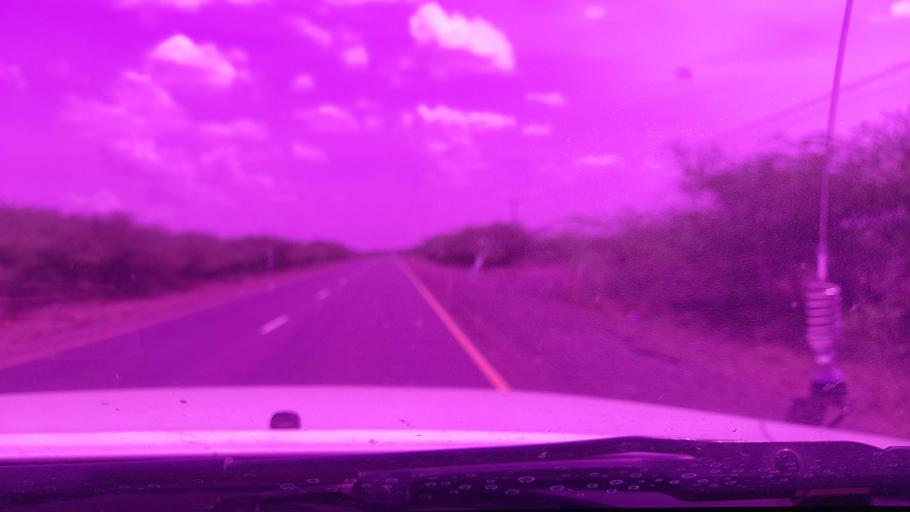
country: ET
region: Afar
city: Awash
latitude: 9.3591
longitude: 40.3054
